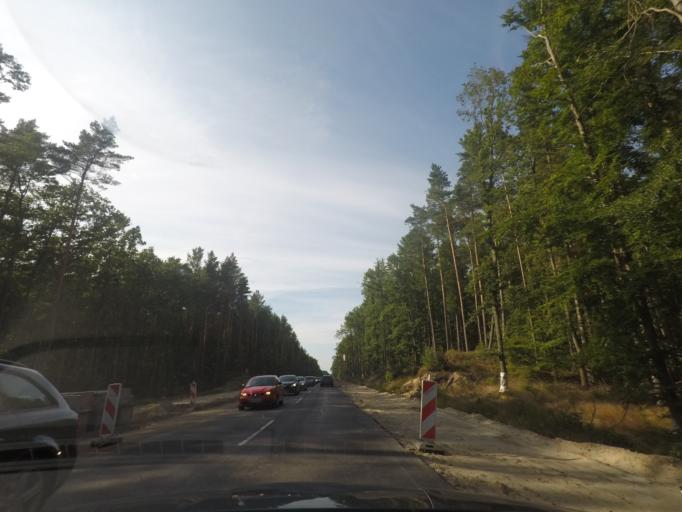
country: PL
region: Pomeranian Voivodeship
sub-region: Powiat leborski
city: Leba
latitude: 54.7069
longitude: 17.5827
